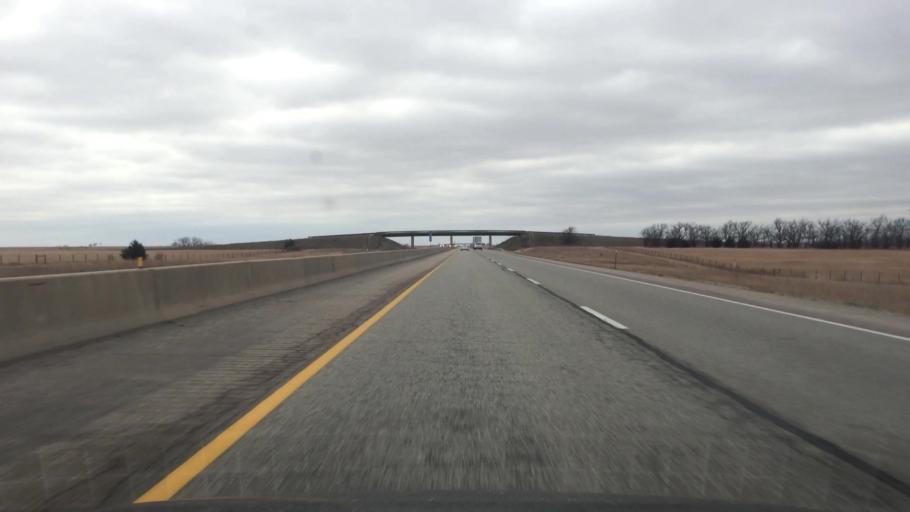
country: US
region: Kansas
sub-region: Butler County
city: El Dorado
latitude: 38.0160
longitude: -96.6736
